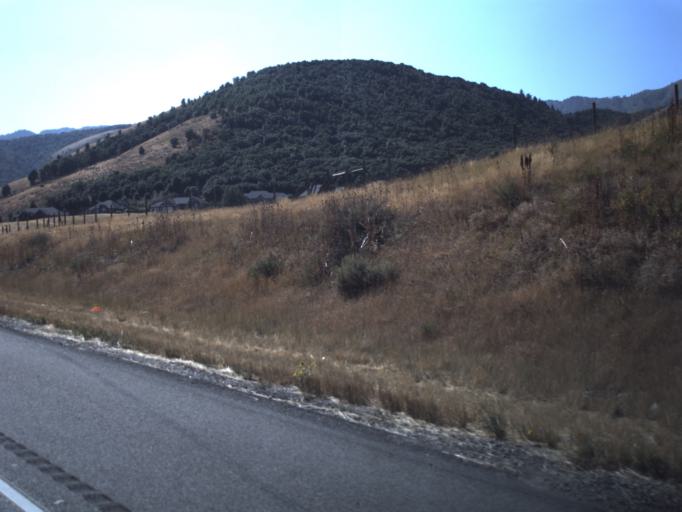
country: US
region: Utah
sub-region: Cache County
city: Wellsville
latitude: 41.6067
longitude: -111.9415
